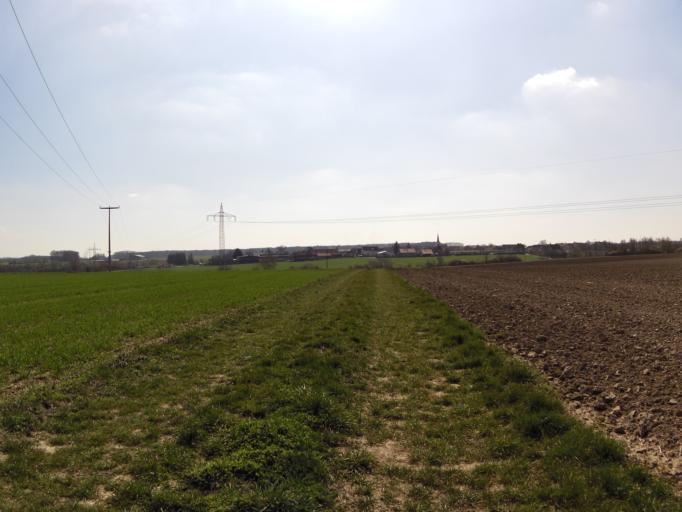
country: DE
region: Bavaria
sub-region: Regierungsbezirk Unterfranken
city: Biebelried
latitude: 49.7367
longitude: 10.0903
